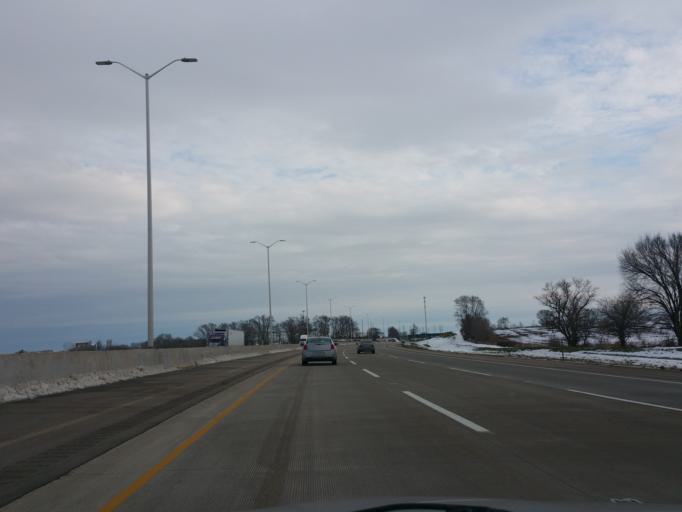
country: US
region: Illinois
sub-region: Winnebago County
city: Cherry Valley
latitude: 42.2458
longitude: -88.9285
